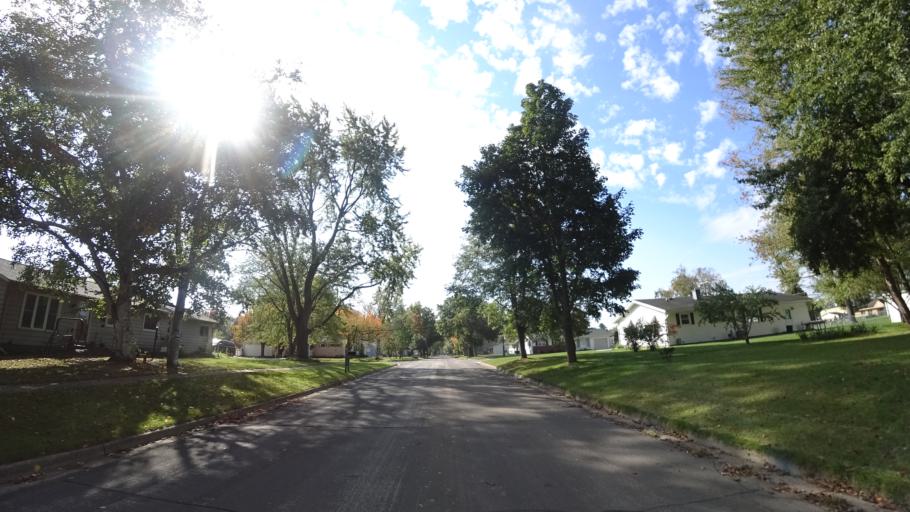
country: US
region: Michigan
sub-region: Saint Joseph County
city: Three Rivers
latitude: 41.9375
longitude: -85.6412
